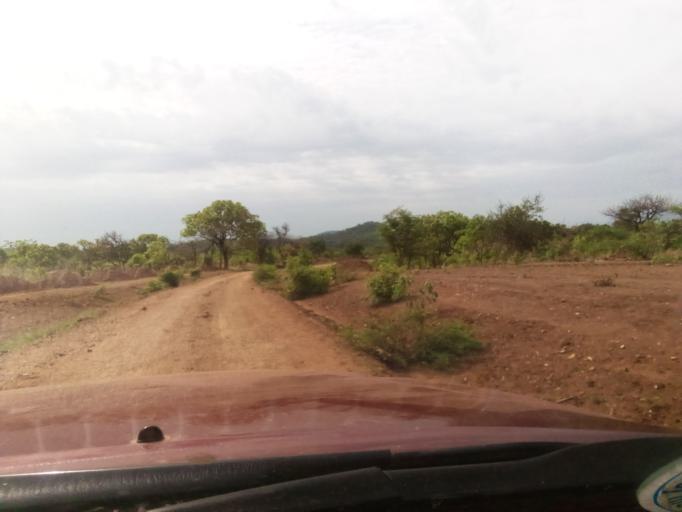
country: ET
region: Oromiya
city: Mendi
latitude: 10.0438
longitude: 35.3043
